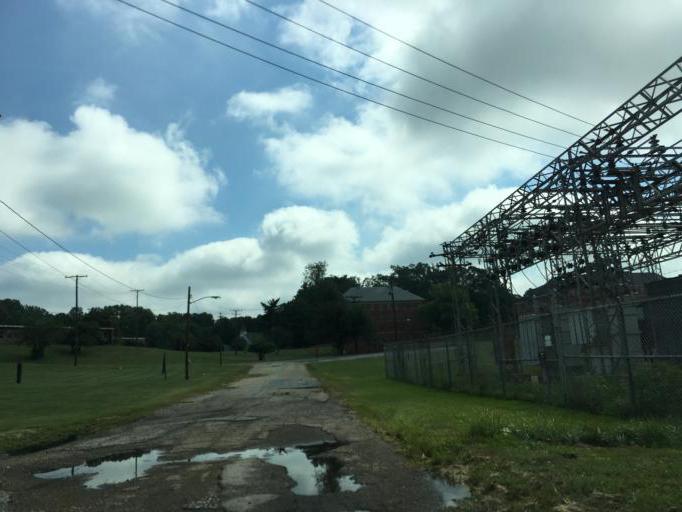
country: US
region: Maryland
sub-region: Anne Arundel County
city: Crownsville
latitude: 39.0248
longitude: -76.6033
